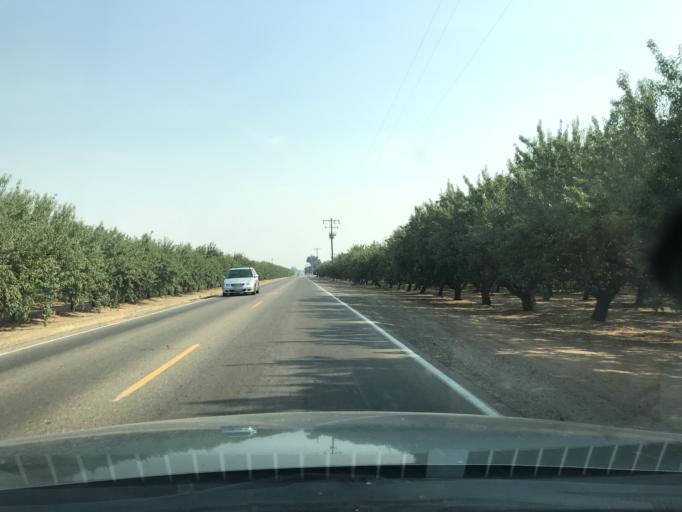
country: US
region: California
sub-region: Merced County
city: Atwater
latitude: 37.3286
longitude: -120.6145
